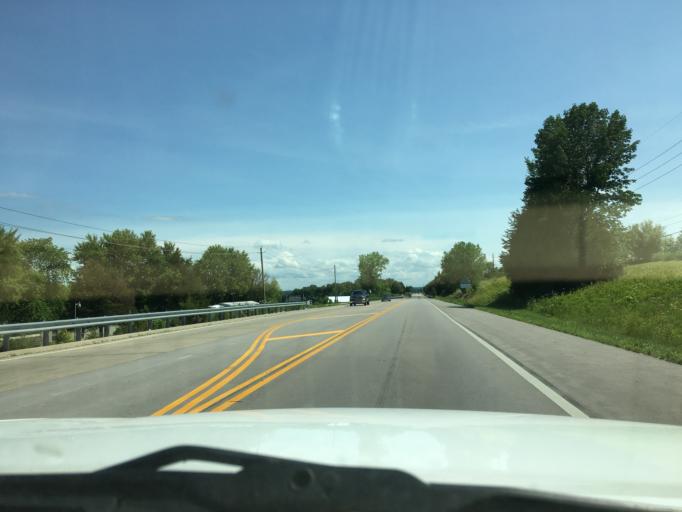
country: US
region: Missouri
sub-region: Franklin County
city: Union
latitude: 38.4815
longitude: -91.0052
